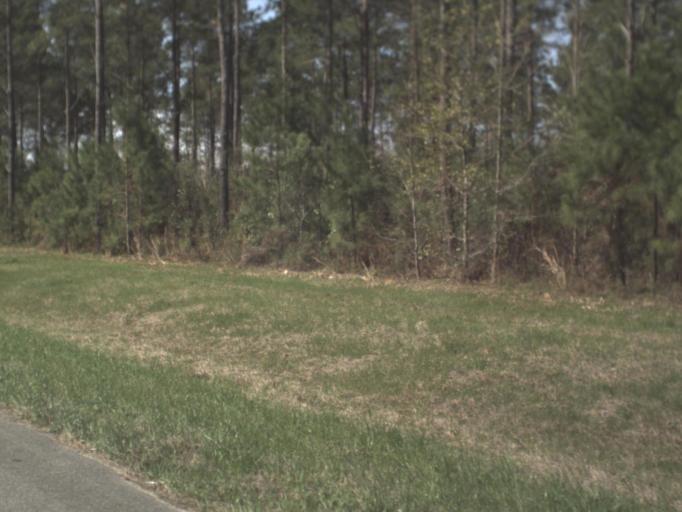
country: US
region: Florida
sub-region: Gadsden County
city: Gretna
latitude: 30.5720
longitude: -84.7057
